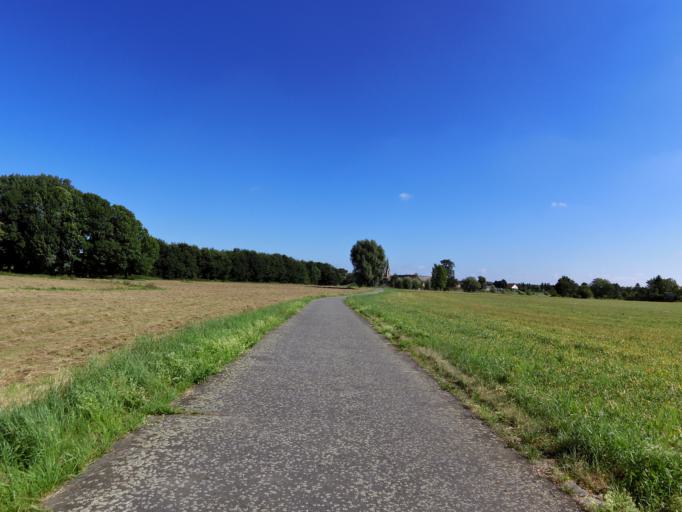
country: DE
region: Saxony
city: Strehla
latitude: 51.3688
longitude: 13.2504
